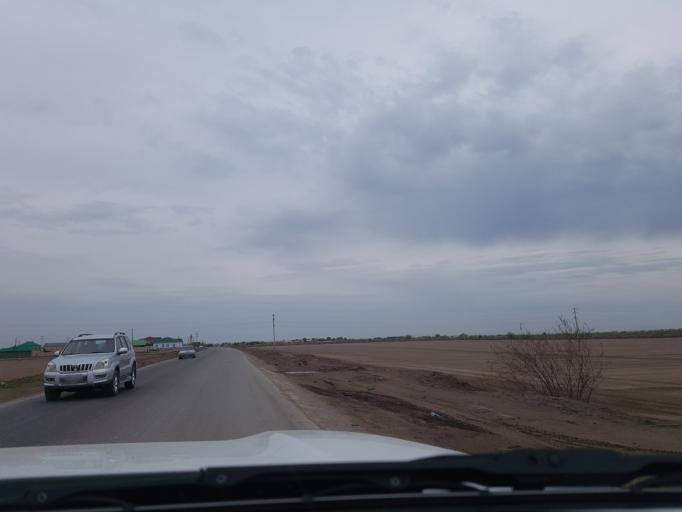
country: TM
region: Lebap
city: Turkmenabat
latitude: 39.0660
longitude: 63.5610
